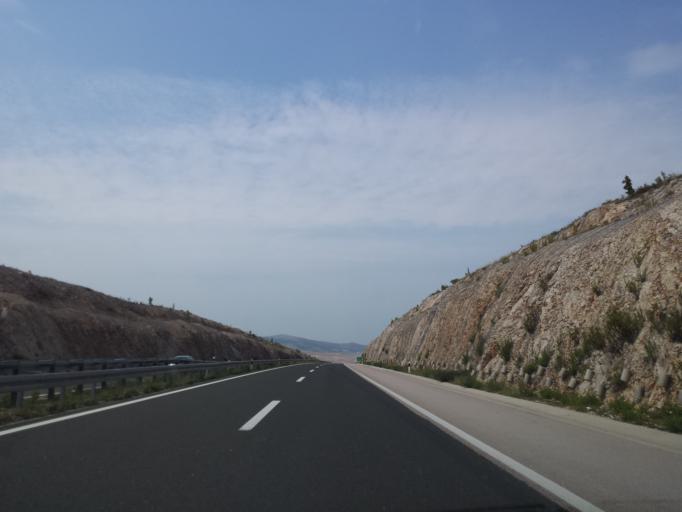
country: HR
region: Zadarska
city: Pridraga
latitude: 44.2411
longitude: 15.5577
